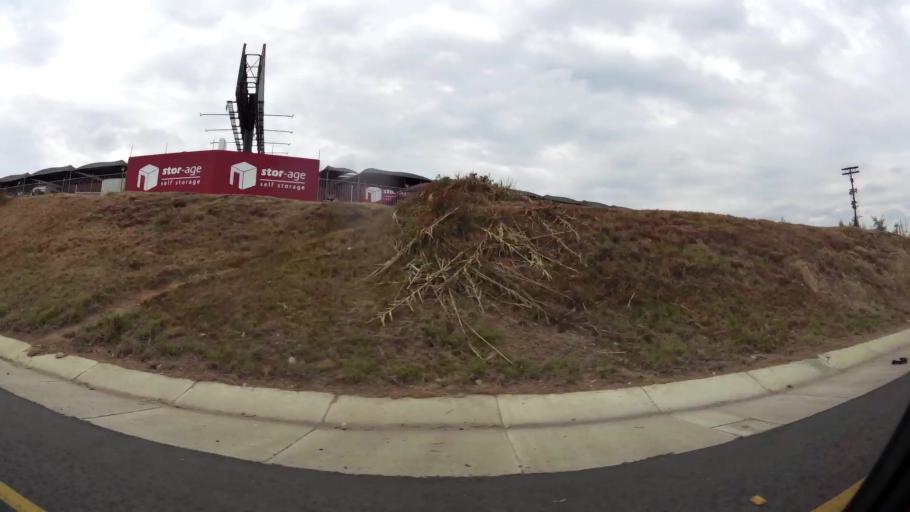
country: ZA
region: Gauteng
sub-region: West Rand District Municipality
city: Muldersdriseloop
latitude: -26.0247
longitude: 27.8524
